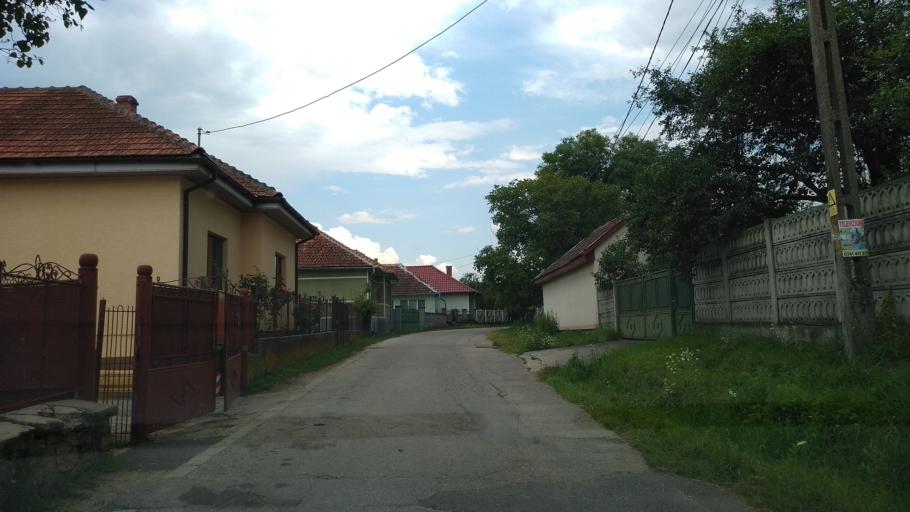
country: RO
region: Hunedoara
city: Salasu de Sus
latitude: 45.5096
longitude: 22.9559
